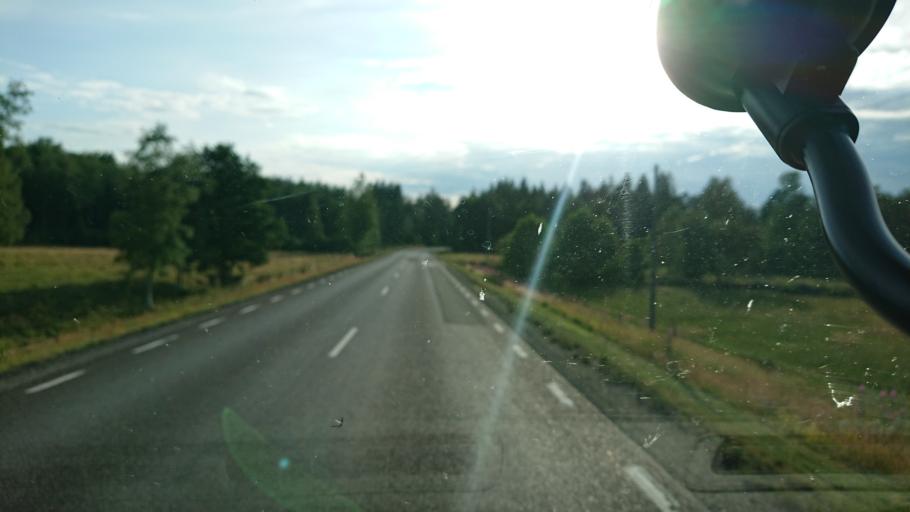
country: SE
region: Kronoberg
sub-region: Vaxjo Kommun
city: Braas
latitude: 57.0227
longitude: 15.0168
